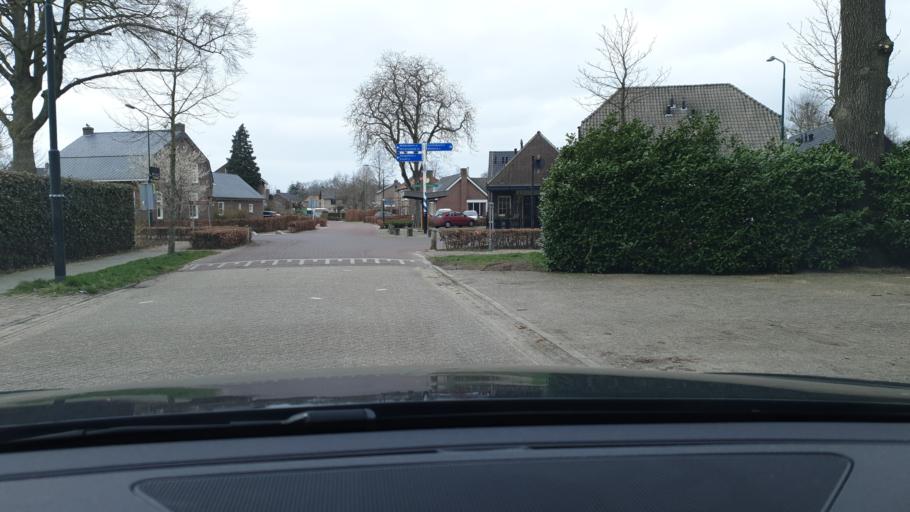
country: NL
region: North Brabant
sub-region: Gemeente Oirschot
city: Oostelbeers
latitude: 51.4201
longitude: 5.2925
